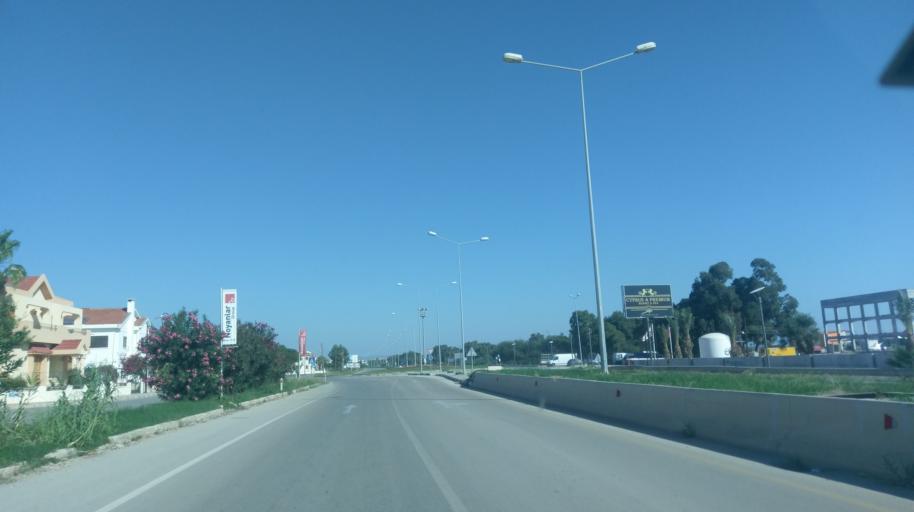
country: CY
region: Ammochostos
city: Trikomo
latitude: 35.2674
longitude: 33.9136
